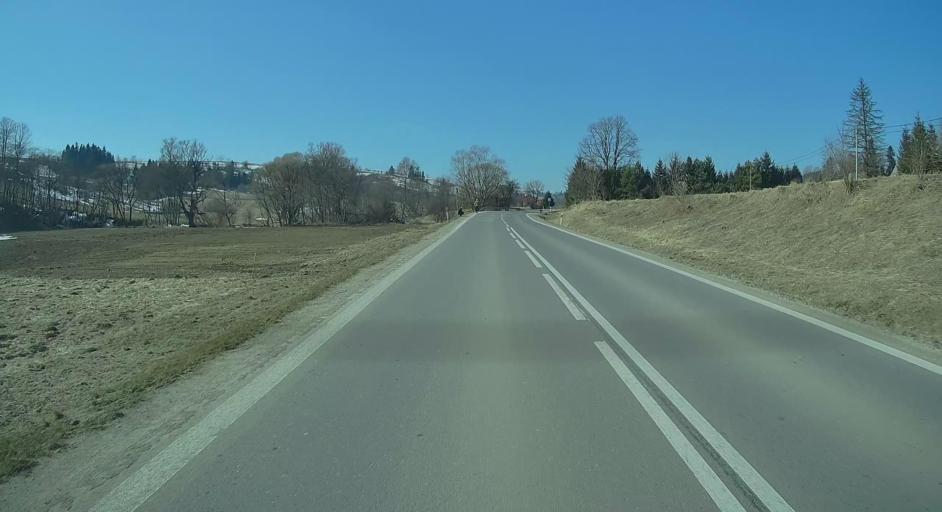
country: PL
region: Subcarpathian Voivodeship
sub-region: Powiat bieszczadzki
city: Ustrzyki Dolne
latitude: 49.4999
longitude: 22.6314
